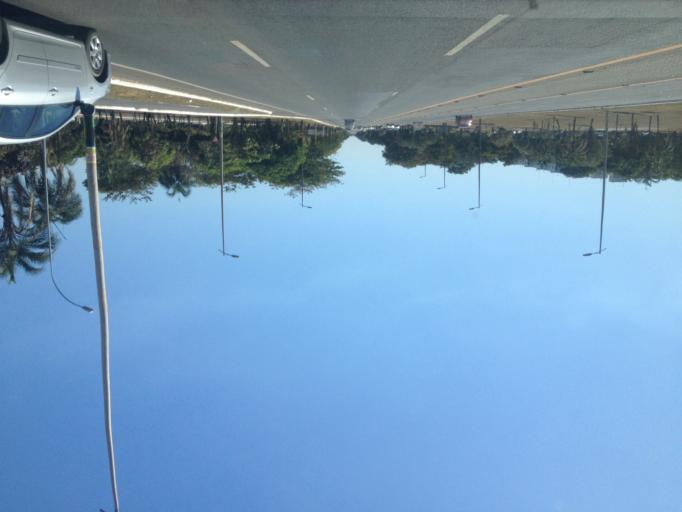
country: BR
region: Federal District
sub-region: Brasilia
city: Brasilia
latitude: -15.8345
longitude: -47.9249
